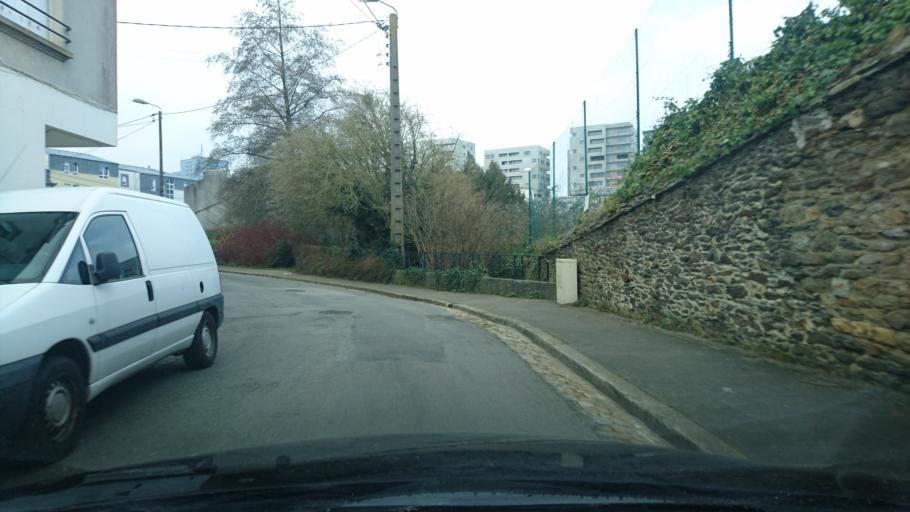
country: FR
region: Brittany
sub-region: Departement du Finistere
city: Brest
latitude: 48.3885
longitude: -4.5008
